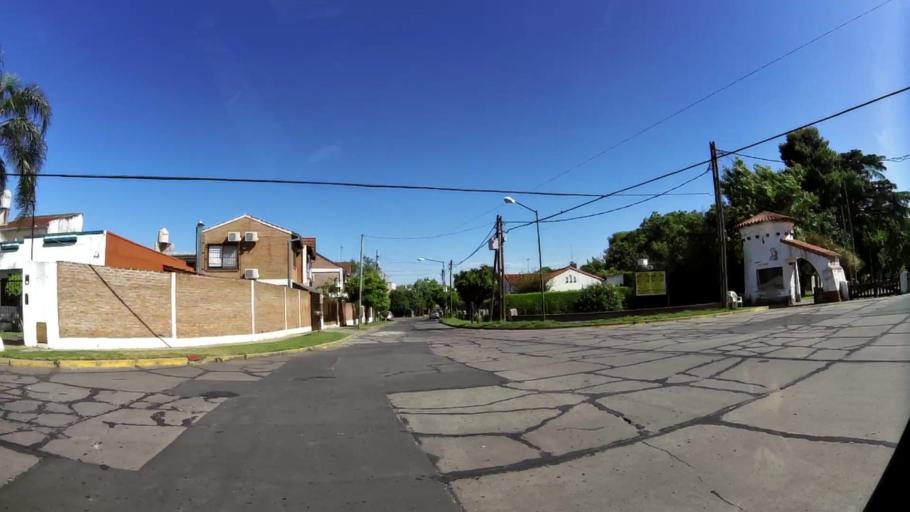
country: AR
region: Buenos Aires
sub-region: Partido de San Isidro
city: San Isidro
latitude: -34.4703
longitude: -58.5293
